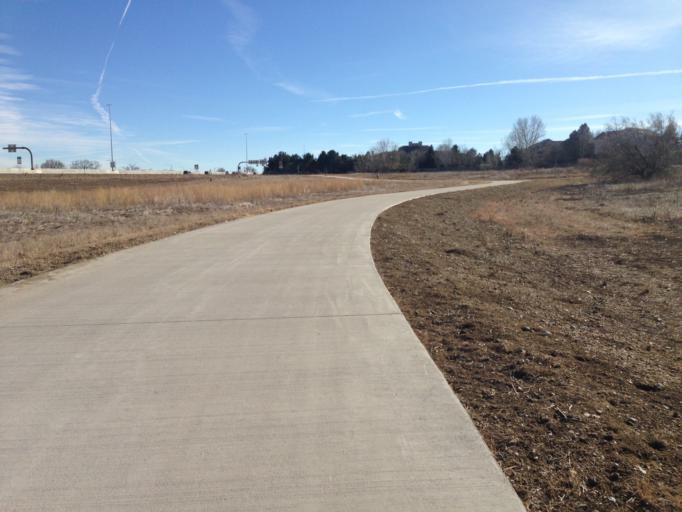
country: US
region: Colorado
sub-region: Broomfield County
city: Broomfield
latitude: 39.8797
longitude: -105.0679
